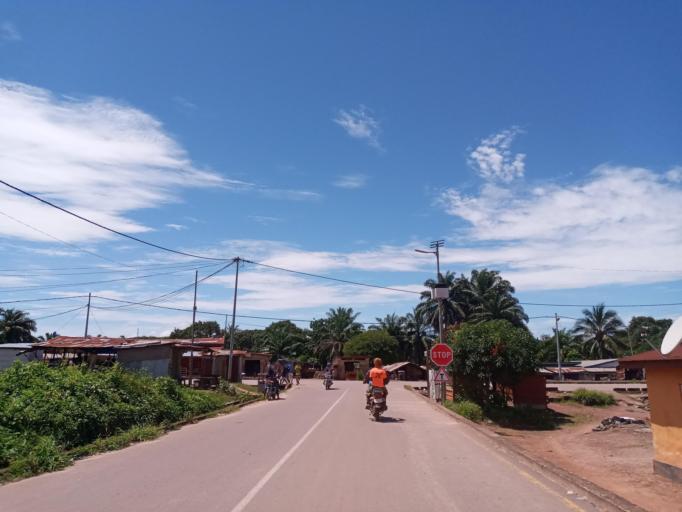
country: SL
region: Eastern Province
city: Koidu
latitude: 8.6466
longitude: -10.9650
